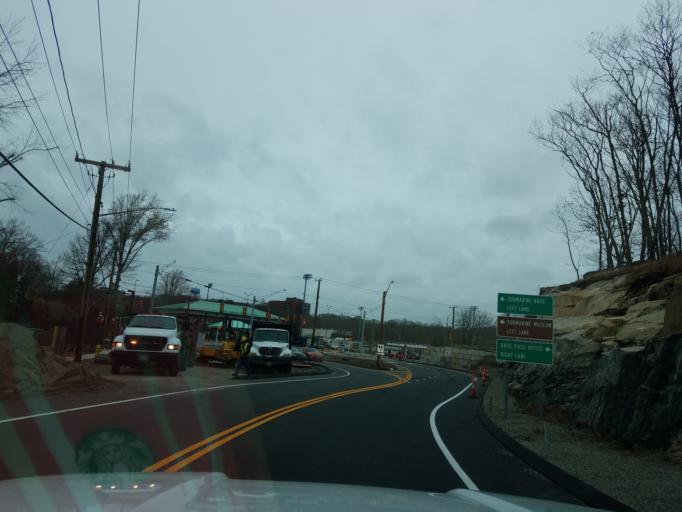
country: US
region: Connecticut
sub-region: New London County
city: Conning Towers-Nautilus Park
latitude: 41.3871
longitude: -72.0862
